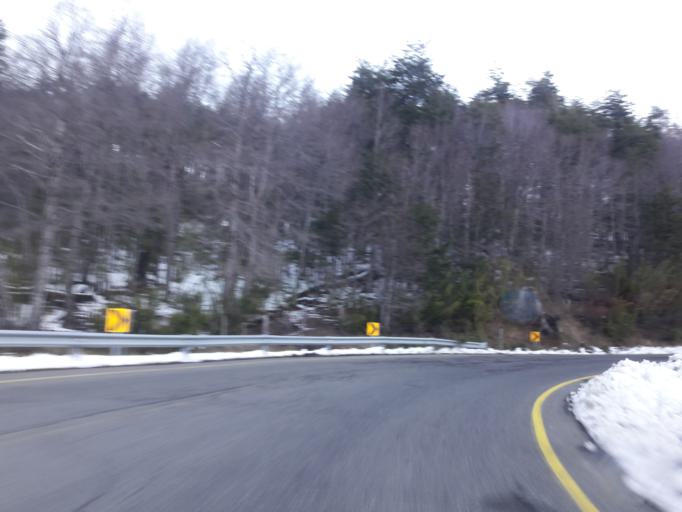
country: CL
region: Araucania
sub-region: Provincia de Cautin
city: Vilcun
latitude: -38.5033
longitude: -71.5195
